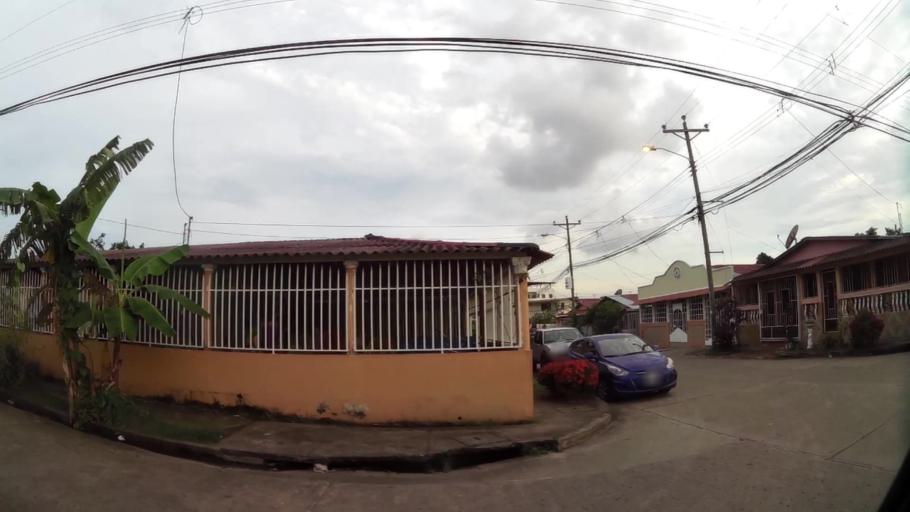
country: PA
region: Panama
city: Tocumen
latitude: 9.0951
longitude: -79.3956
